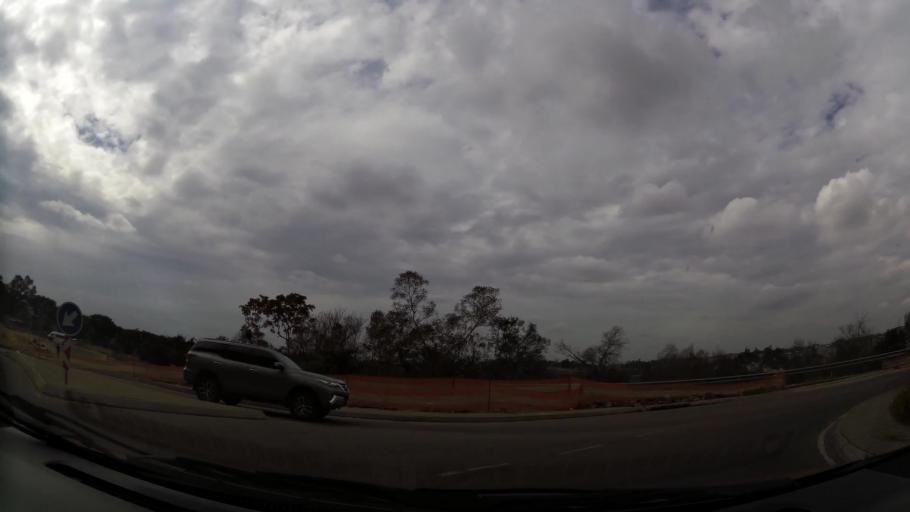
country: ZA
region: Gauteng
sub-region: West Rand District Municipality
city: Muldersdriseloop
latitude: -26.0614
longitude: 27.8392
